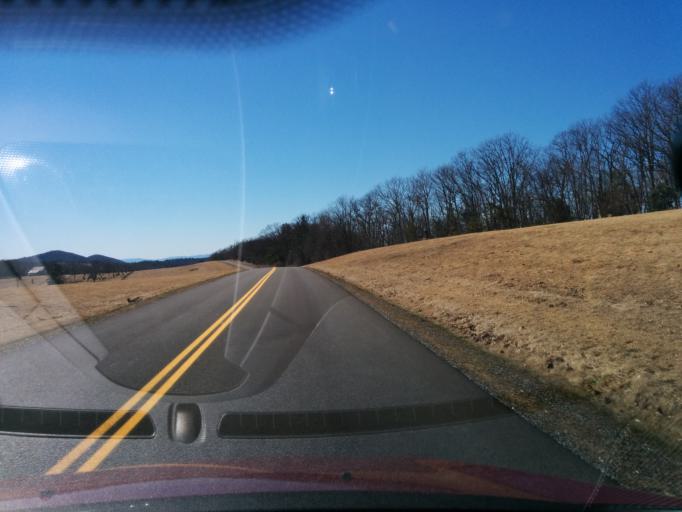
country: US
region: Virginia
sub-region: Augusta County
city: Stuarts Draft
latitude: 37.9035
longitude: -79.1076
